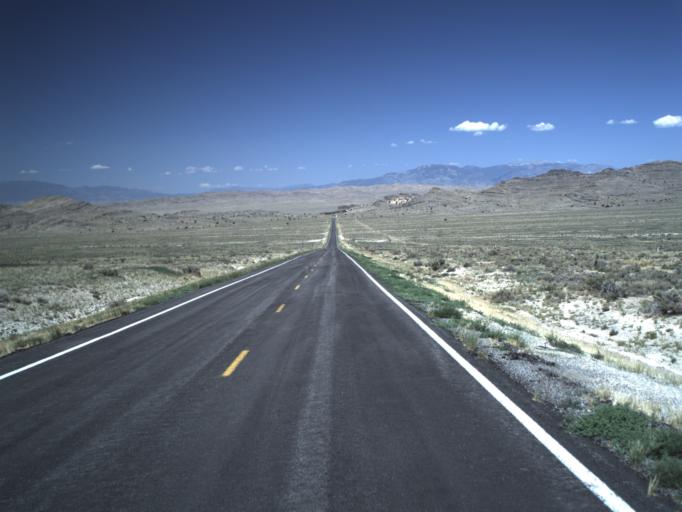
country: US
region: Utah
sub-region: Beaver County
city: Milford
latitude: 39.0735
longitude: -113.6681
